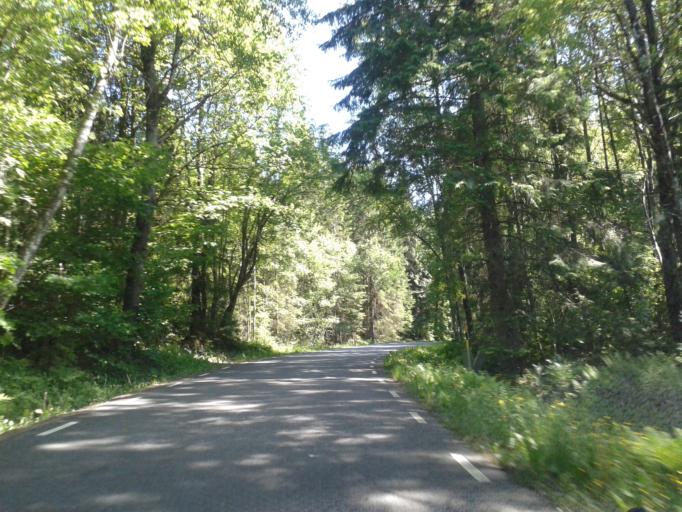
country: SE
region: Vaestra Goetaland
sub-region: Kungalvs Kommun
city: Diserod
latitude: 57.9705
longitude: 11.9884
